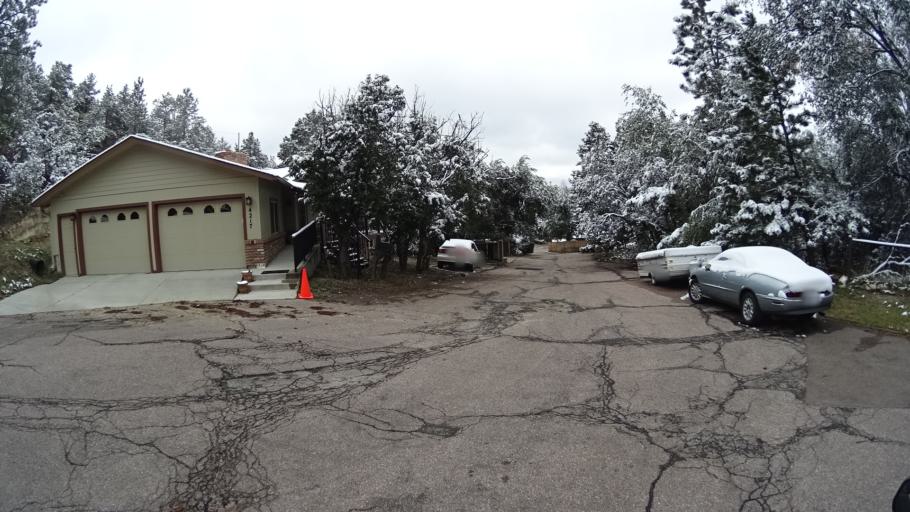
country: US
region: Colorado
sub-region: El Paso County
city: Colorado Springs
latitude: 38.8936
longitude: -104.7776
